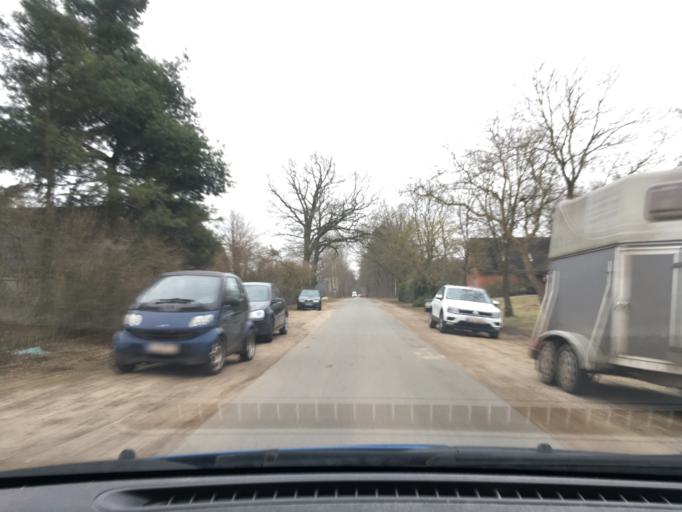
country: DE
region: Lower Saxony
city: Vogelsen
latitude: 53.2880
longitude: 10.3434
